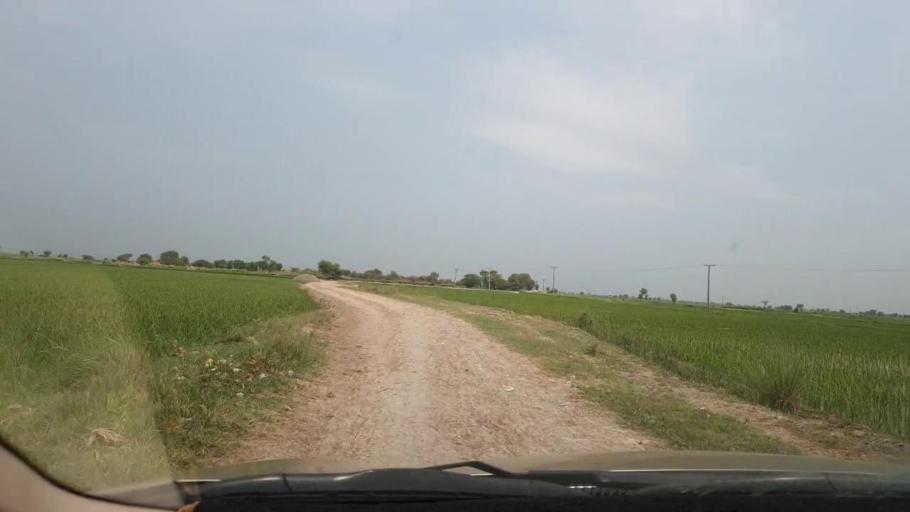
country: PK
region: Sindh
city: Goth Garelo
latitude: 27.5193
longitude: 68.1224
